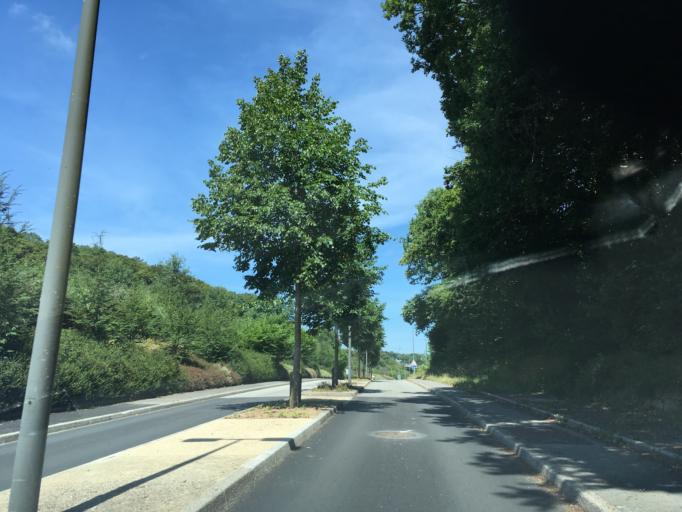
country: FR
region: Brittany
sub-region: Departement du Finistere
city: Quimper
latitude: 48.0105
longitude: -4.1204
